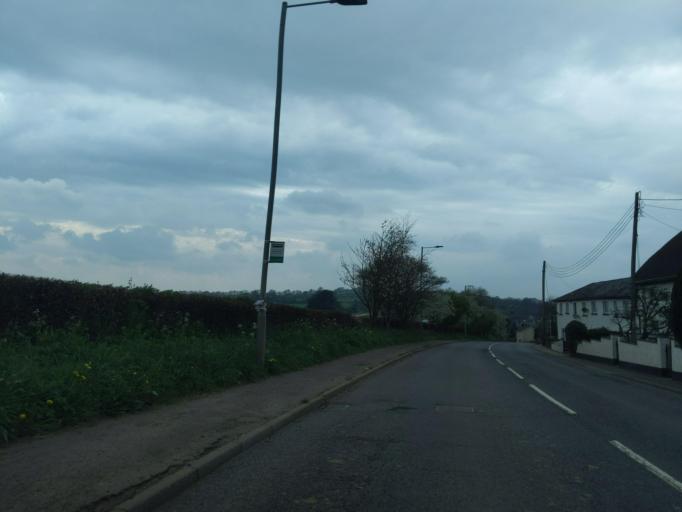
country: GB
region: England
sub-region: Devon
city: Crediton
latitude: 50.8090
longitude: -3.7411
